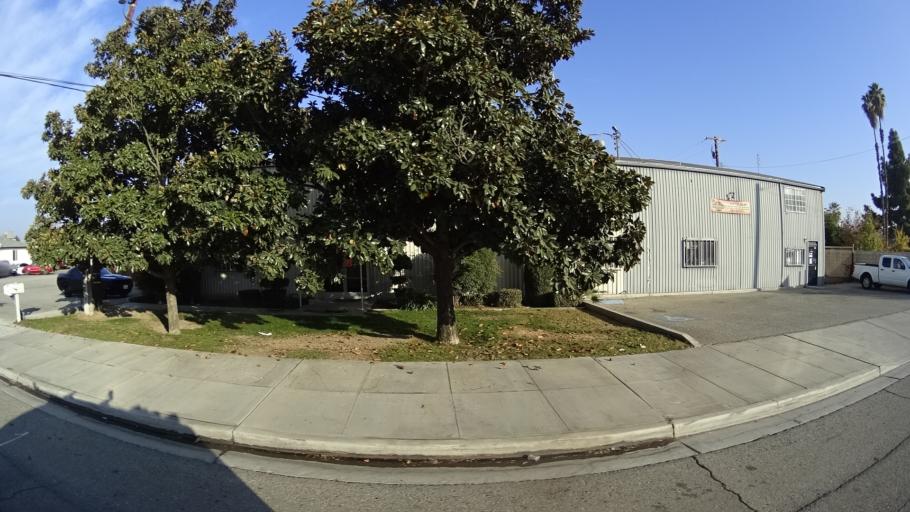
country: US
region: California
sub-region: Kern County
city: Rosedale
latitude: 35.3836
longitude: -119.1432
